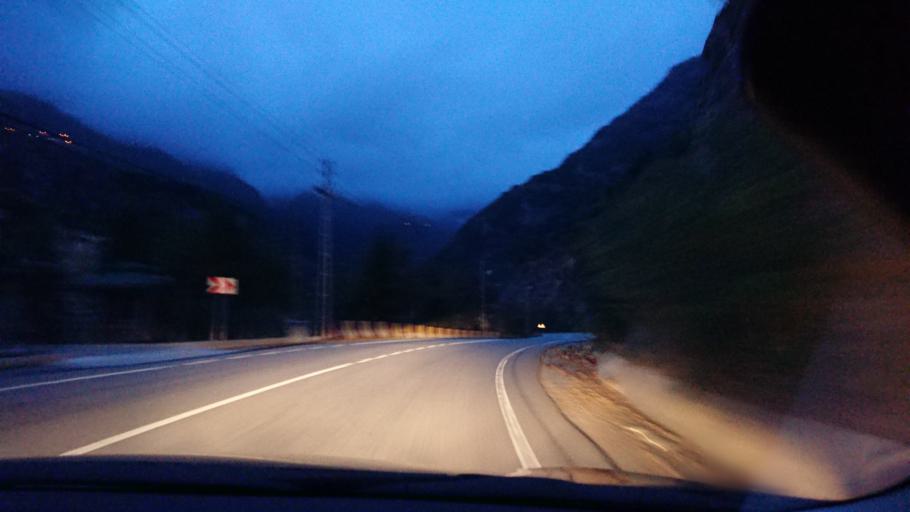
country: TR
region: Gumushane
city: Kurtun
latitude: 40.6762
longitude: 39.1411
